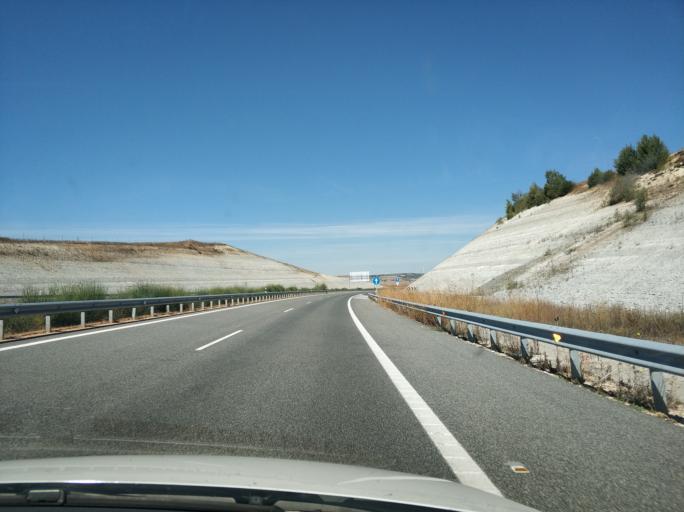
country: ES
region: Castille and Leon
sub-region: Provincia de Burgos
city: Sotragero
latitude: 42.3910
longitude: -3.6958
